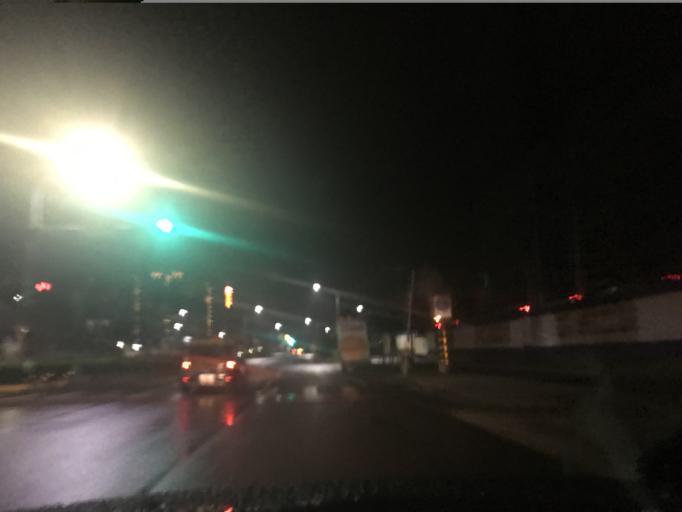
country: TW
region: Taiwan
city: Daxi
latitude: 24.9248
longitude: 121.2818
